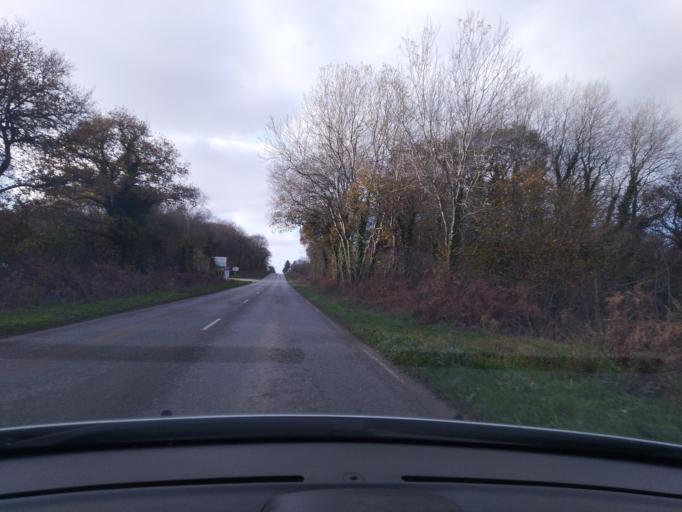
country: FR
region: Brittany
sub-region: Departement du Finistere
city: Plouigneau
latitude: 48.5718
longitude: -3.7260
